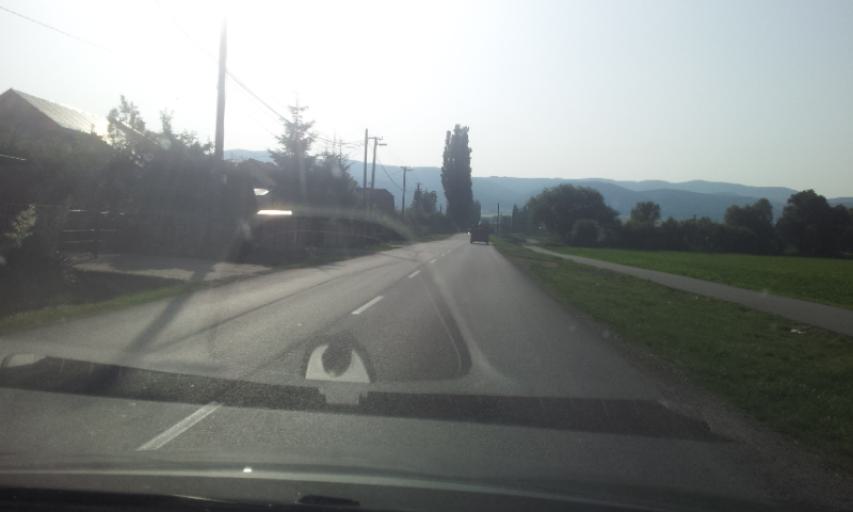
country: SK
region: Kosicky
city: Kosice
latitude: 48.6068
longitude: 21.3335
